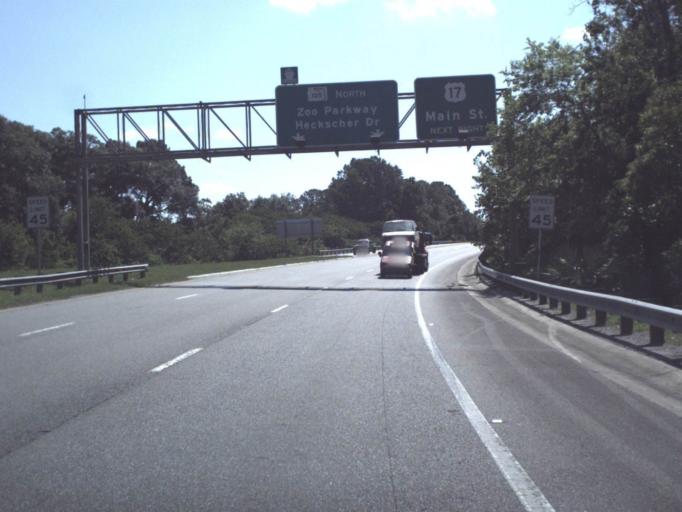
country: US
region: Florida
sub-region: Duval County
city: Jacksonville
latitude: 30.4074
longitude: -81.6535
